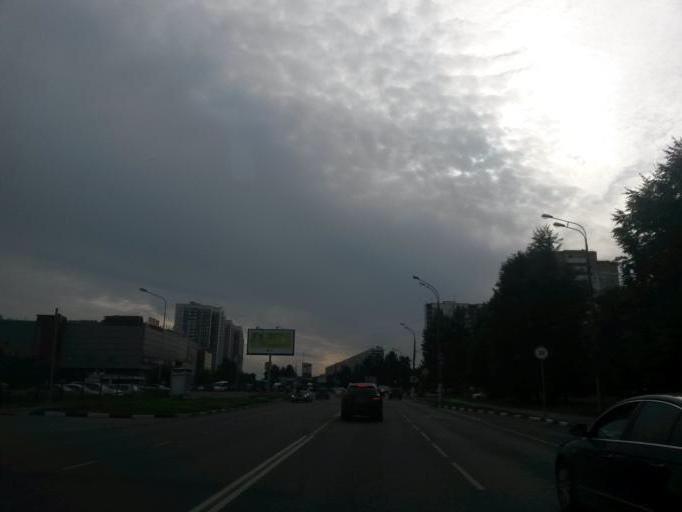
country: RU
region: Moscow
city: Orekhovo-Borisovo
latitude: 55.6137
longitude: 37.7375
